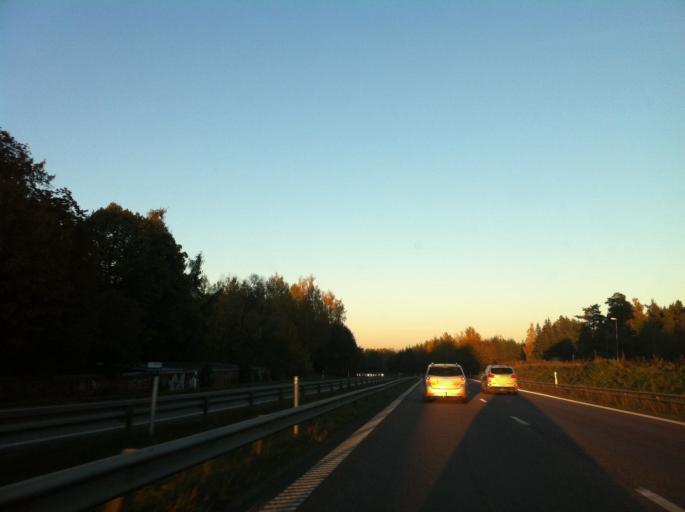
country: SE
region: Gaevleborg
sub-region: Gavle Kommun
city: Valbo
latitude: 60.6330
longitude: 16.9999
